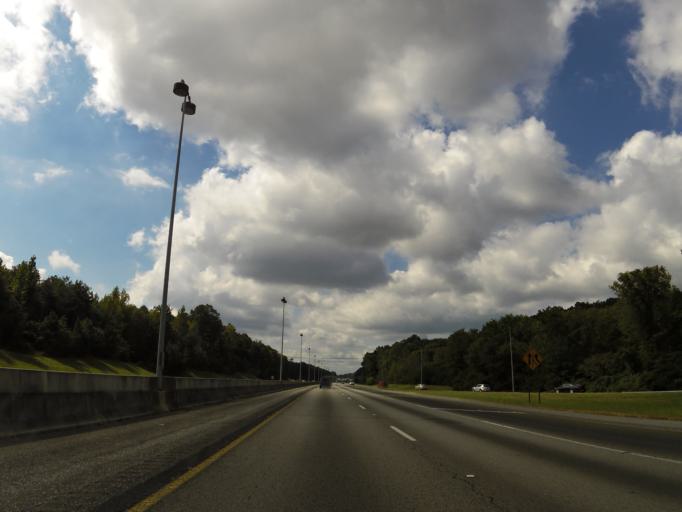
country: US
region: Alabama
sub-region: Jefferson County
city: Bessemer
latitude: 33.3364
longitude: -87.0344
